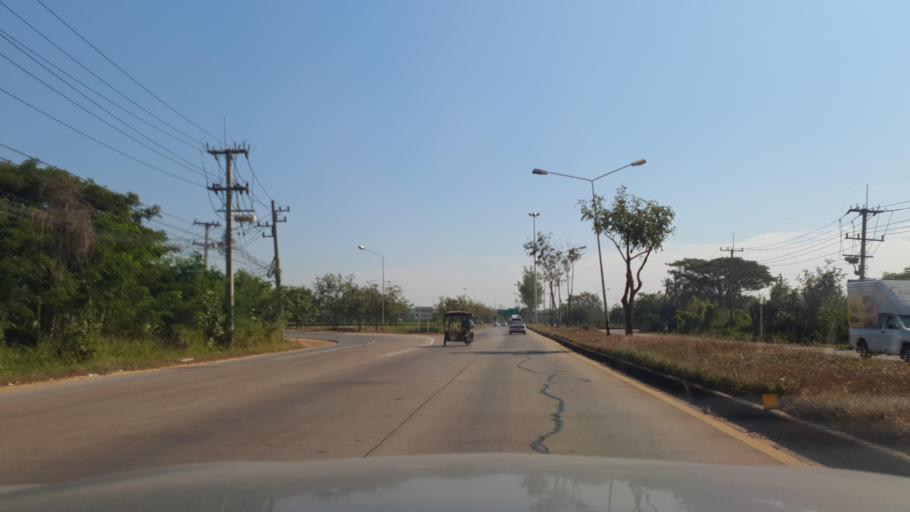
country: TH
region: Khon Kaen
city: Khon Kaen
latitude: 16.4376
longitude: 102.9138
